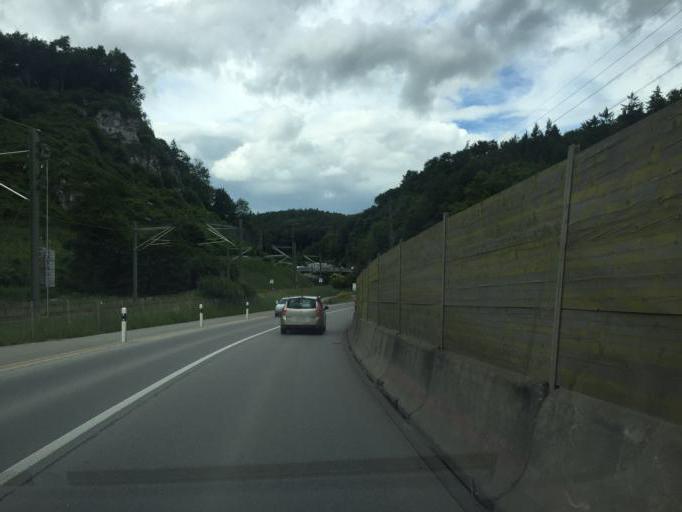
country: CH
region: Schaffhausen
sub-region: Bezirk Schaffhausen
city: Neuhausen
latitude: 47.6907
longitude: 8.6087
